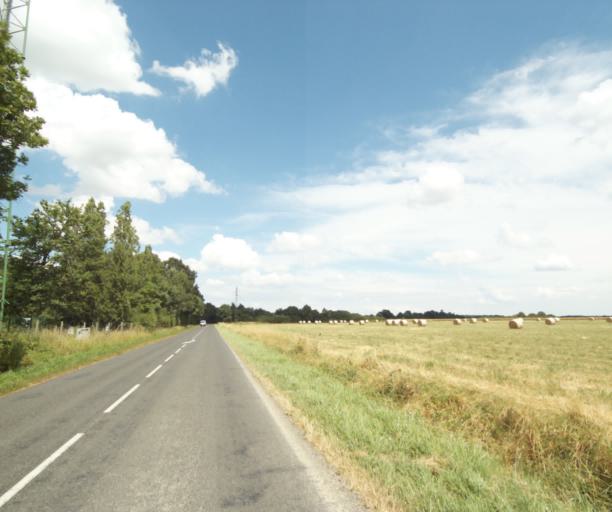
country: FR
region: Ile-de-France
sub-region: Departement de Seine-et-Marne
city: Vulaines-sur-Seine
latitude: 48.4381
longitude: 2.7739
